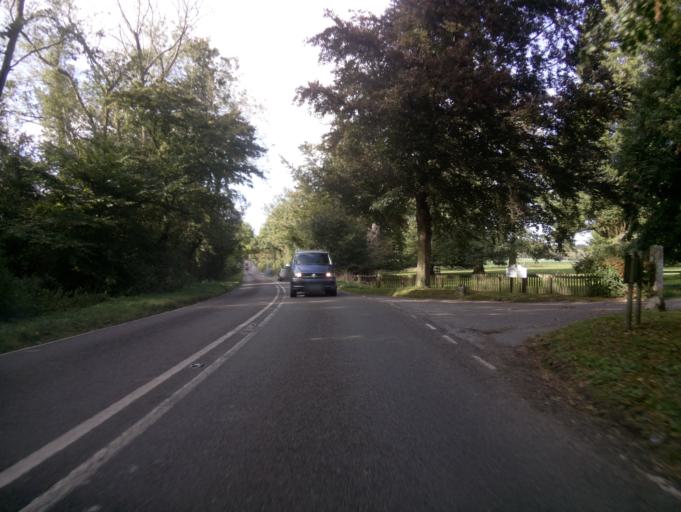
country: GB
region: England
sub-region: Hampshire
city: Old Basing
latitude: 51.2107
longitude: -1.0527
